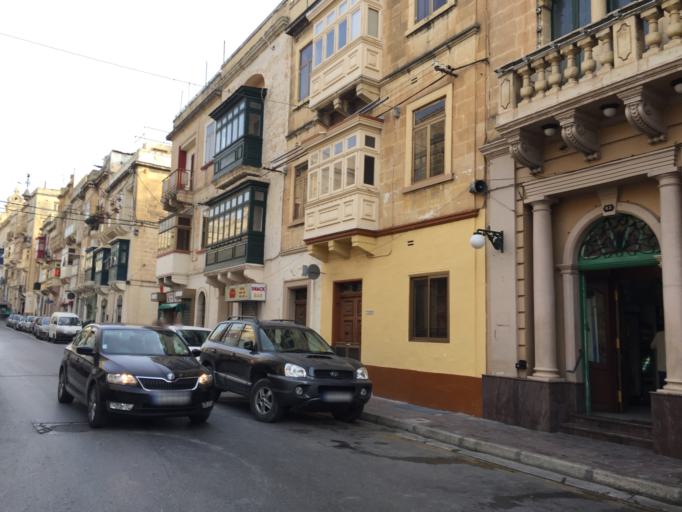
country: MT
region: L-Isla
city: Senglea
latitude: 35.8876
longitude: 14.5169
